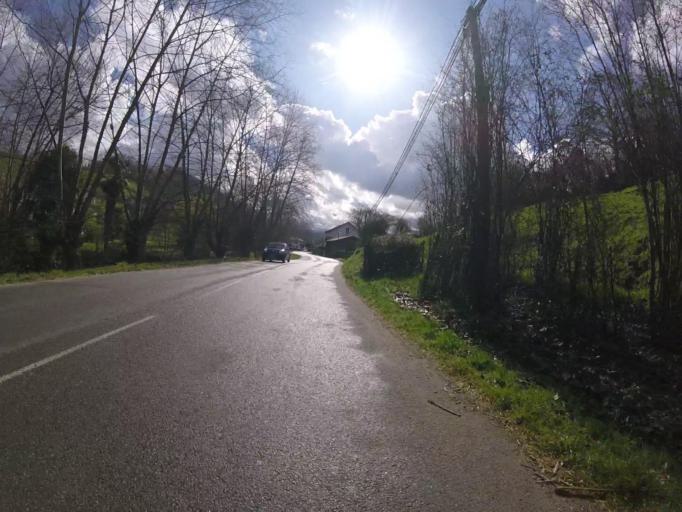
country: FR
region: Aquitaine
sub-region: Departement des Pyrenees-Atlantiques
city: Sare
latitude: 43.3020
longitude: -1.5744
